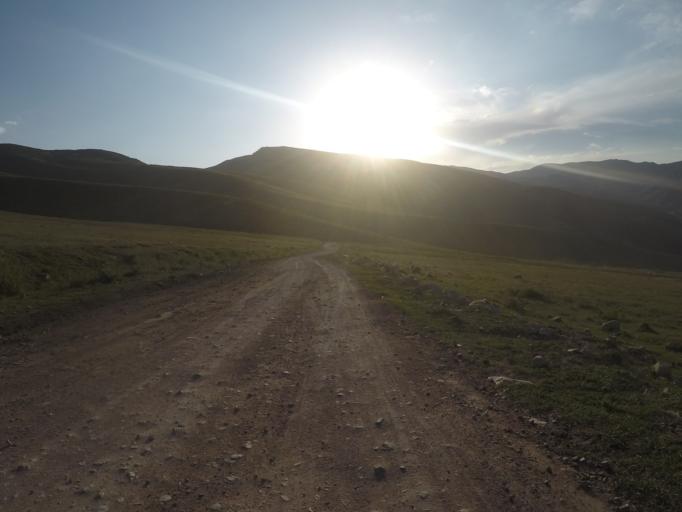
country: KG
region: Chuy
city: Bishkek
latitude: 42.6533
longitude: 74.6576
